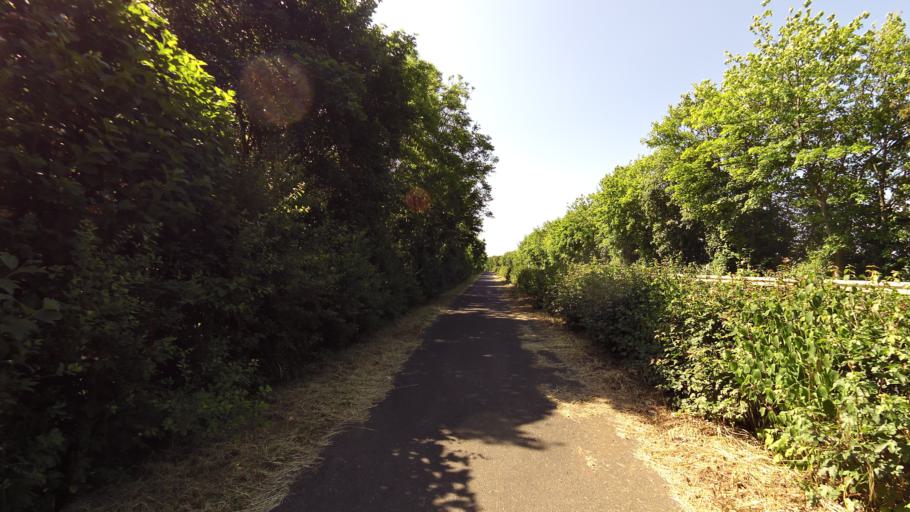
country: DE
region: North Rhine-Westphalia
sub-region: Regierungsbezirk Koln
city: Rheinbach
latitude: 50.6444
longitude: 6.9483
